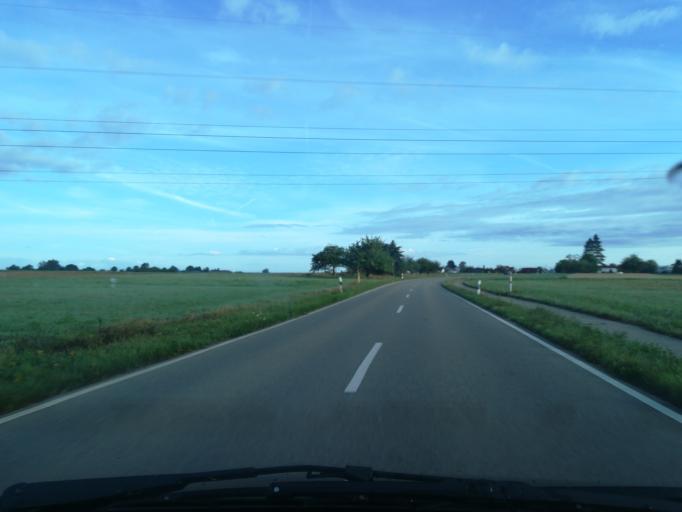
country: DE
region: Baden-Wuerttemberg
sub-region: Tuebingen Region
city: Sickenhausen
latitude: 48.5131
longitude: 9.1772
